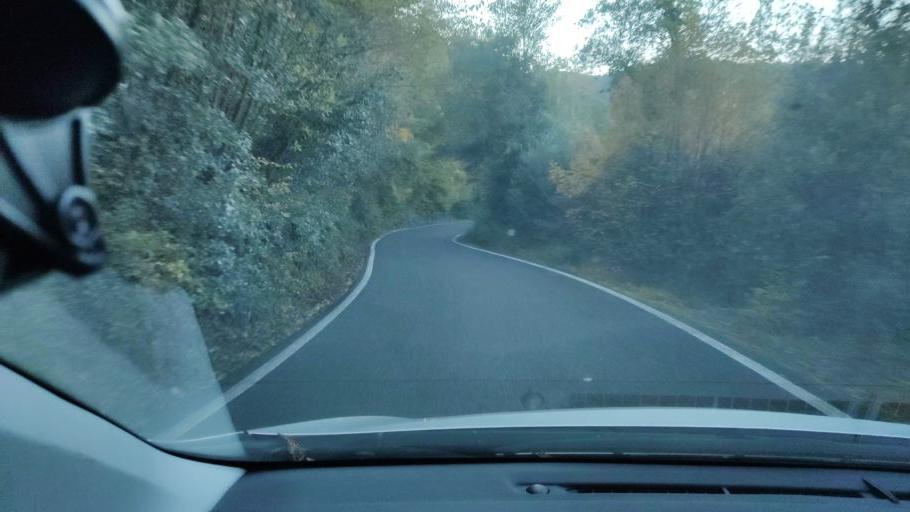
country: IT
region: Umbria
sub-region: Provincia di Terni
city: Amelia
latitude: 42.5864
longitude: 12.4314
